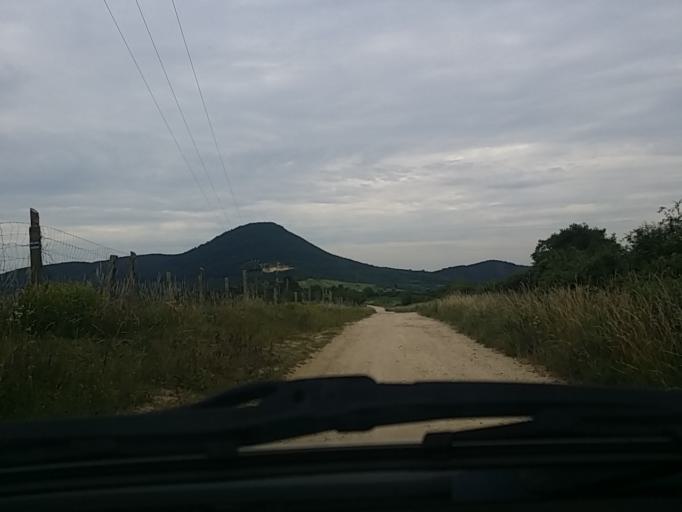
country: HU
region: Pest
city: Csobanka
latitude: 47.6436
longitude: 18.9505
